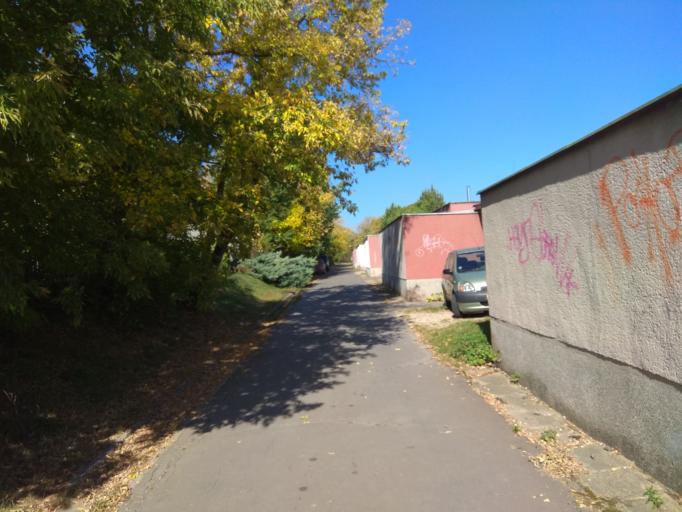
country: SK
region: Kosicky
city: Kosice
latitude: 48.7215
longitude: 21.2431
